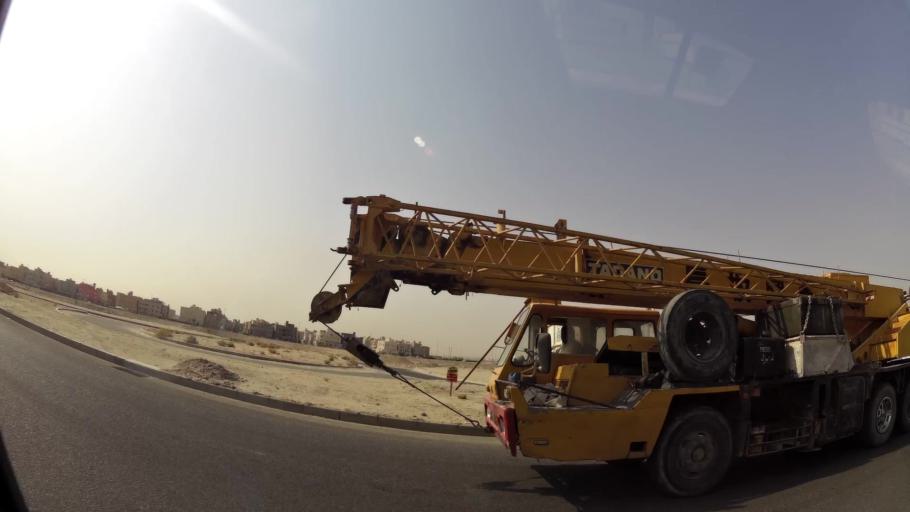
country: KW
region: Muhafazat al Jahra'
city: Al Jahra'
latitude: 29.3450
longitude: 47.7647
